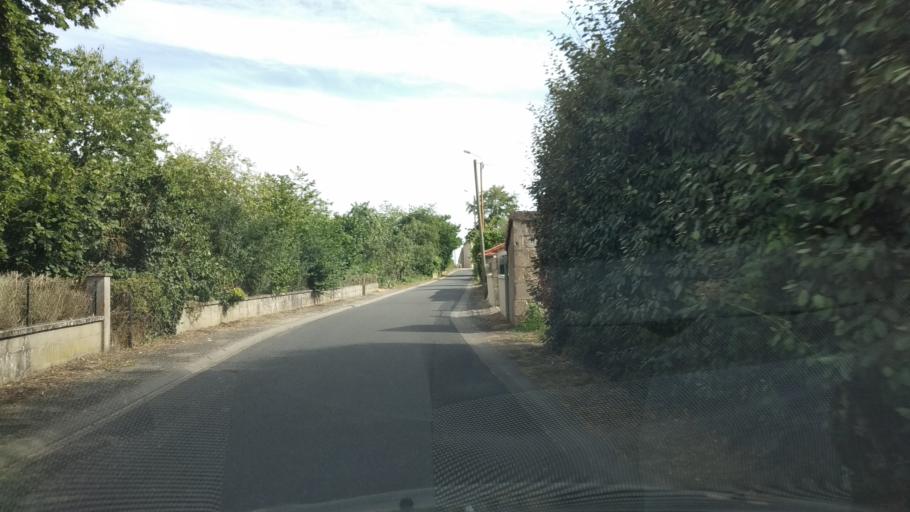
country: FR
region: Poitou-Charentes
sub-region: Departement de la Vienne
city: Chauvigny
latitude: 46.4805
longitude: 0.6479
